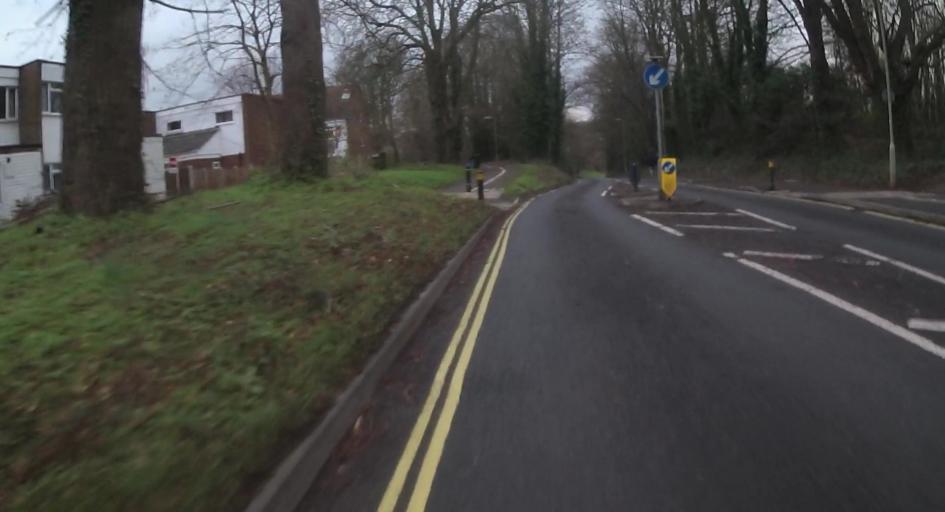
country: GB
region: England
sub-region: Hampshire
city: Basingstoke
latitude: 51.2636
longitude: -1.0727
